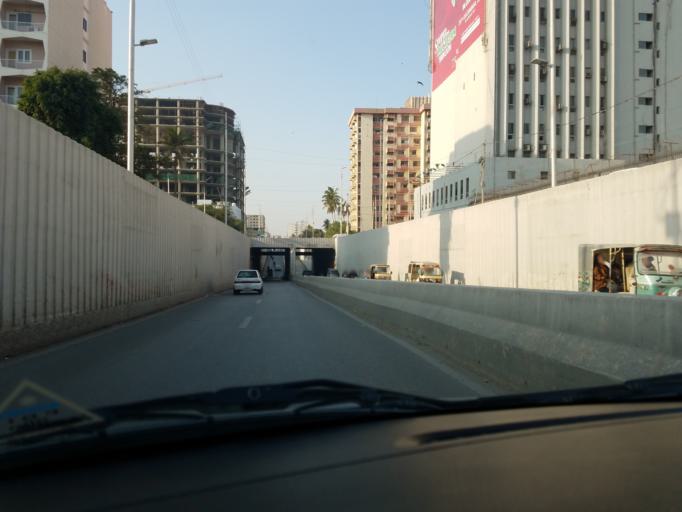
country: PK
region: Sindh
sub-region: Karachi District
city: Karachi
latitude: 24.8515
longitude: 67.0347
